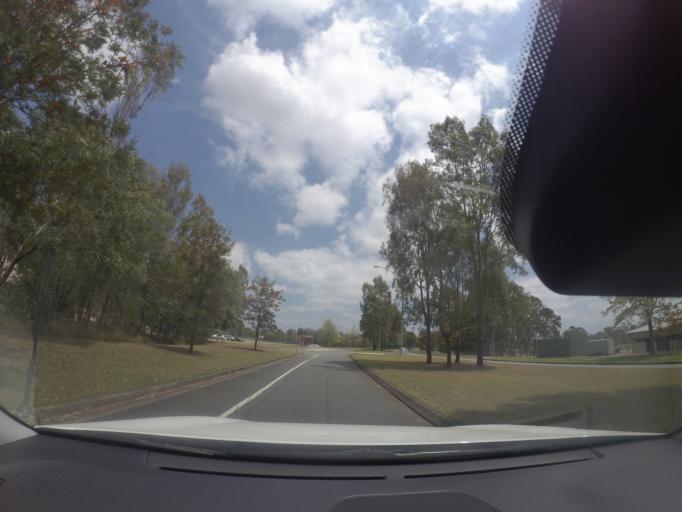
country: AU
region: Queensland
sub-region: Logan
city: Slacks Creek
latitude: -27.6647
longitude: 153.1500
